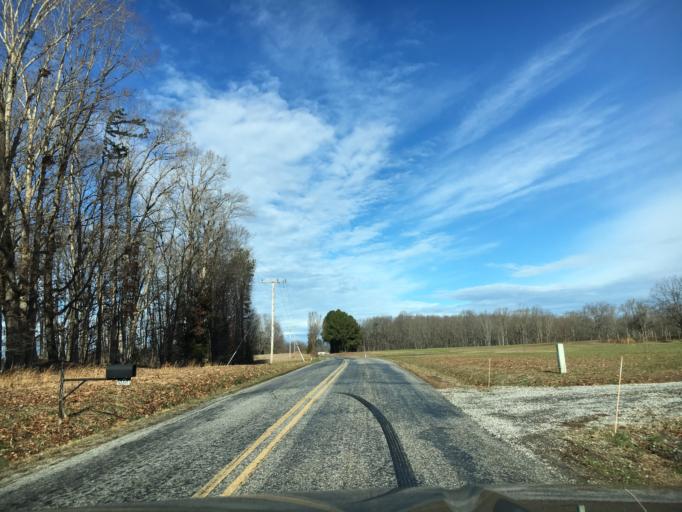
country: US
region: Virginia
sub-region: Cumberland County
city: Cumberland
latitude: 37.3629
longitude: -78.1561
